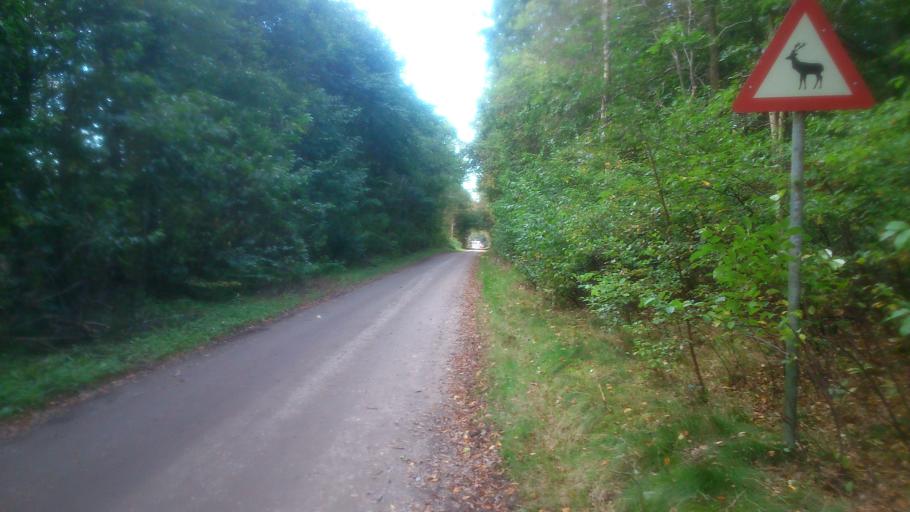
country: DK
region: Central Jutland
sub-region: Holstebro Kommune
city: Ulfborg
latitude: 56.1591
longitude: 8.4096
